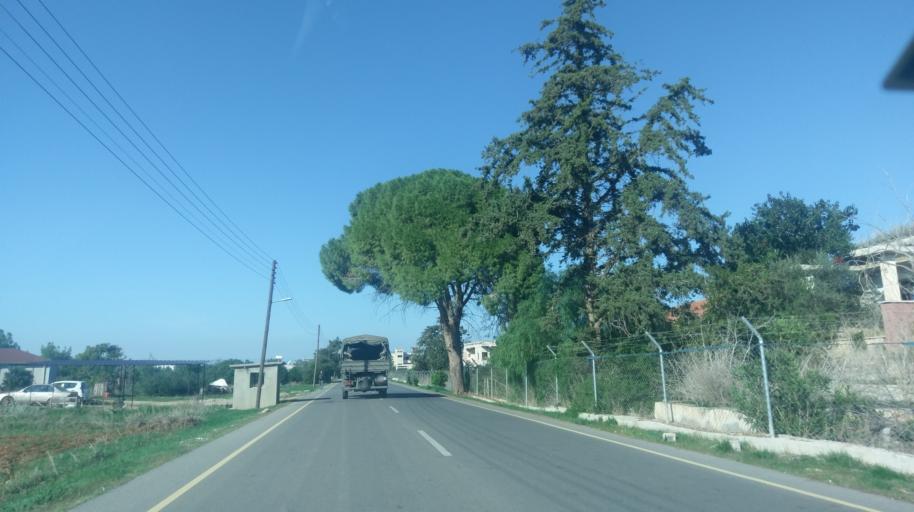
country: CY
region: Ammochostos
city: Deryneia
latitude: 35.0922
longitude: 33.9527
